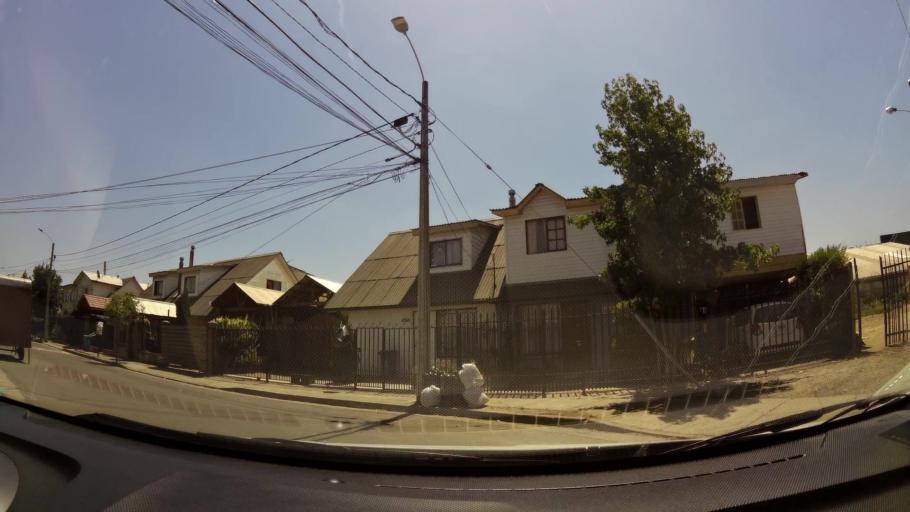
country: CL
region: Maule
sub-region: Provincia de Talca
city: Talca
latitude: -35.4345
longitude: -71.6322
